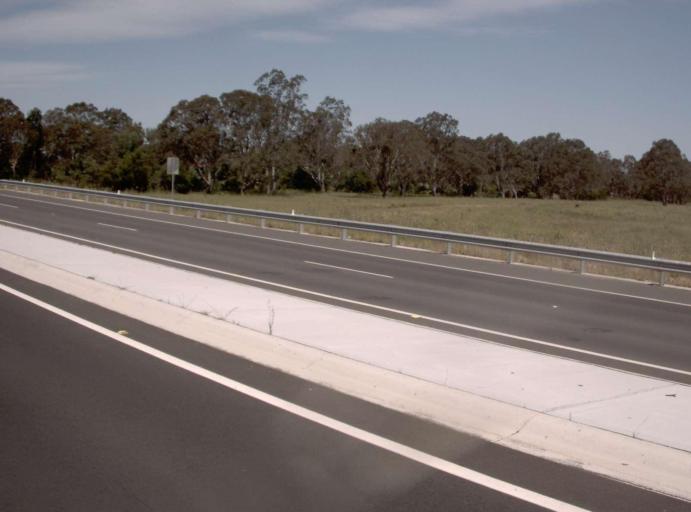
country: AU
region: Victoria
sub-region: Wellington
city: Sale
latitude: -38.1127
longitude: 147.0473
